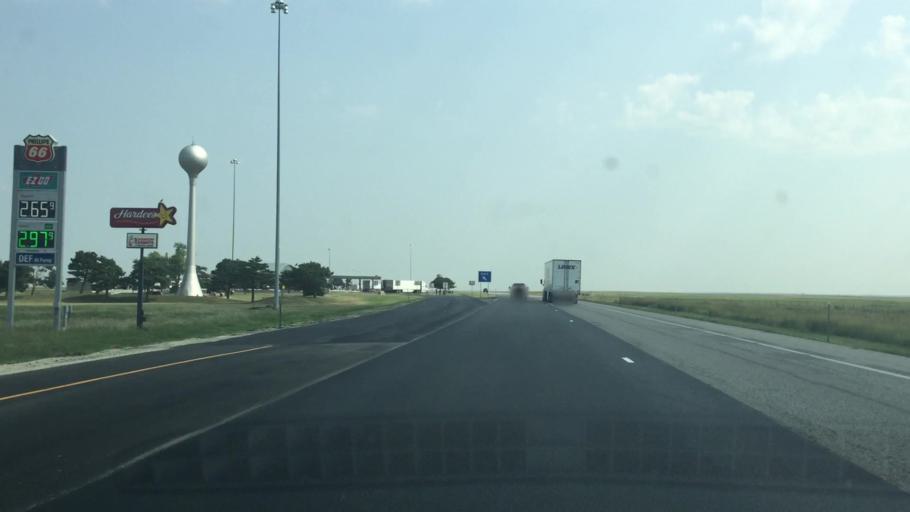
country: US
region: Kansas
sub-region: Chase County
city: Cottonwood Falls
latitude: 38.0924
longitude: -96.5807
